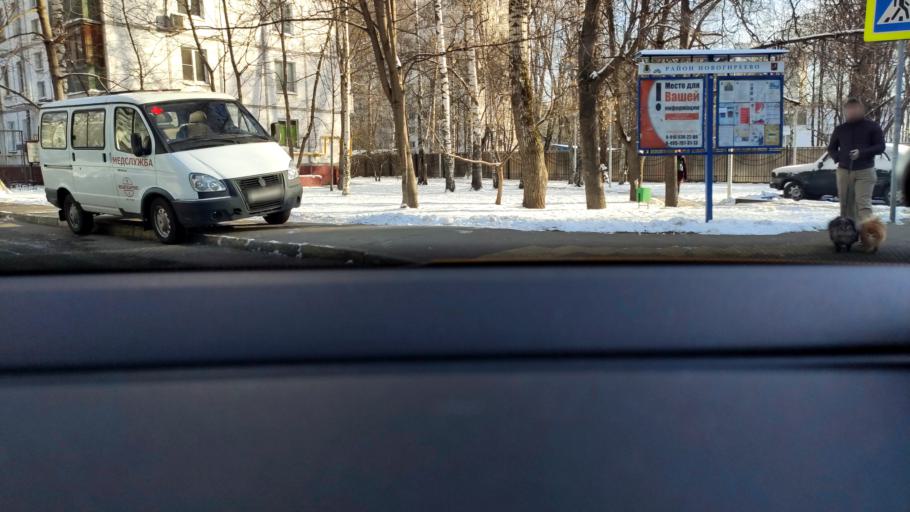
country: RU
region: Moscow
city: Perovo
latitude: 55.7475
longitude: 37.7926
